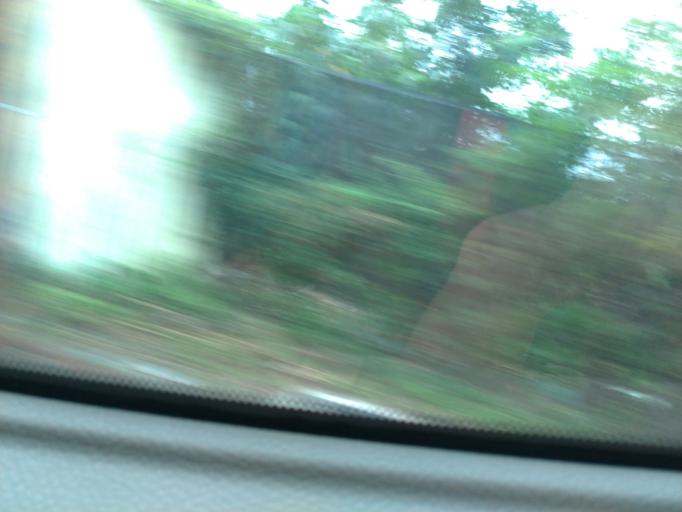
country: TW
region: Taiwan
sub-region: Taoyuan
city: Taoyuan
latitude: 24.9349
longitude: 121.4003
